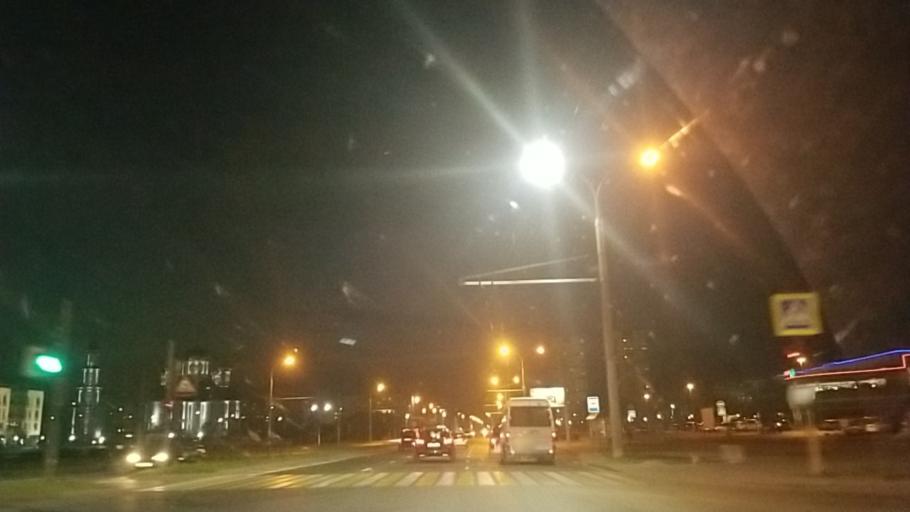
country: BY
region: Brest
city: Brest
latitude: 52.0959
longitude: 23.7660
